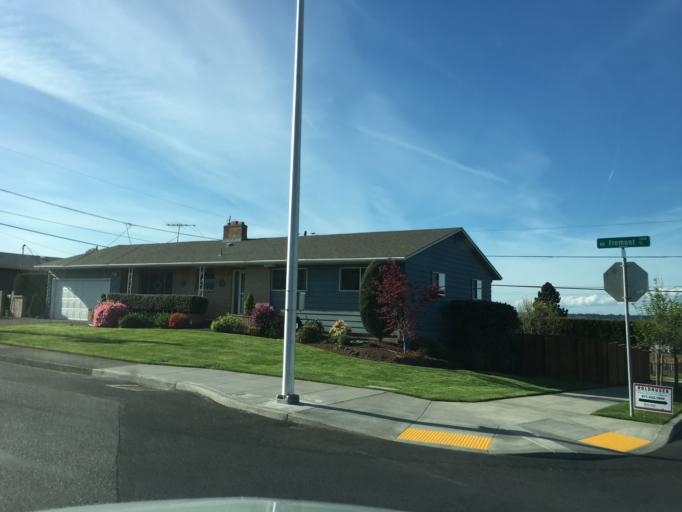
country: US
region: Oregon
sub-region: Multnomah County
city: Lents
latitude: 45.5481
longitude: -122.5321
